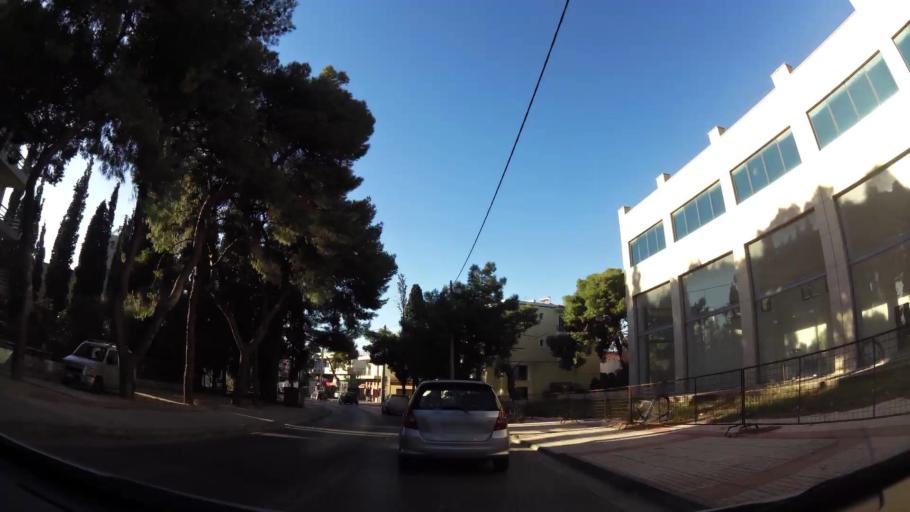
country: GR
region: Attica
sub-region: Nomarchia Athinas
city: Lykovrysi
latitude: 38.0627
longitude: 23.7825
